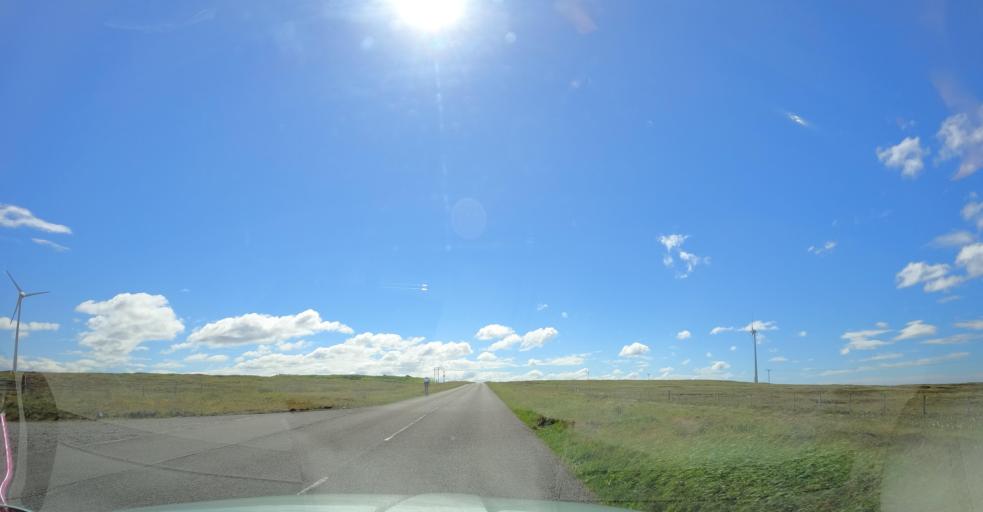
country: GB
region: Scotland
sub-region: Eilean Siar
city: Isle of Lewis
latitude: 58.3851
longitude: -6.4965
